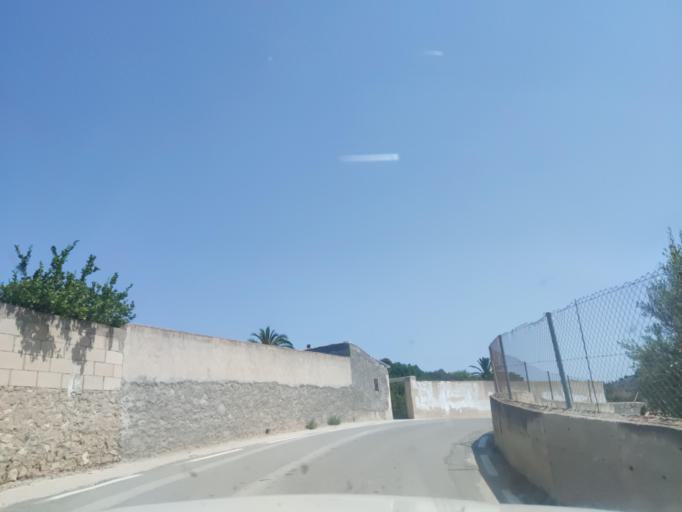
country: ES
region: Murcia
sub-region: Murcia
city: Ulea
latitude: 38.1394
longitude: -1.3186
